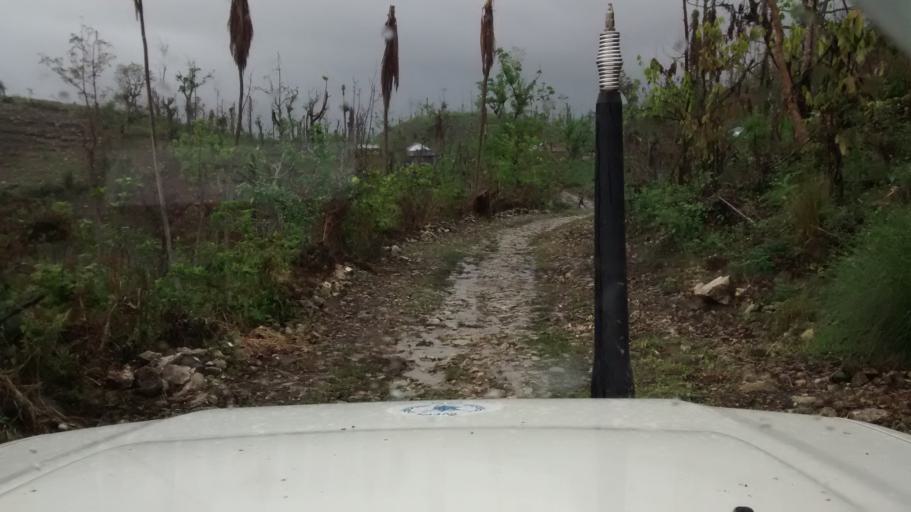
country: HT
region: Grandans
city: Moron
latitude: 18.5277
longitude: -74.1552
